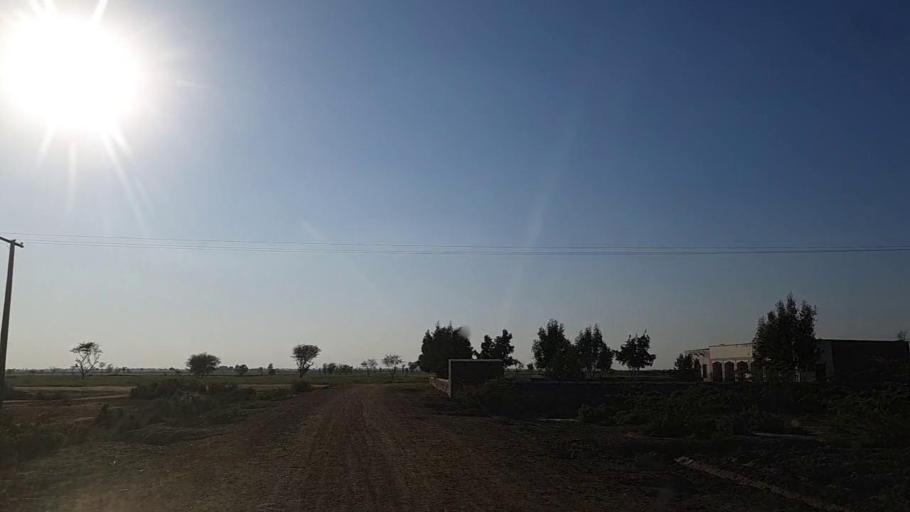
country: PK
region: Sindh
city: Samaro
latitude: 25.3493
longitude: 69.3641
